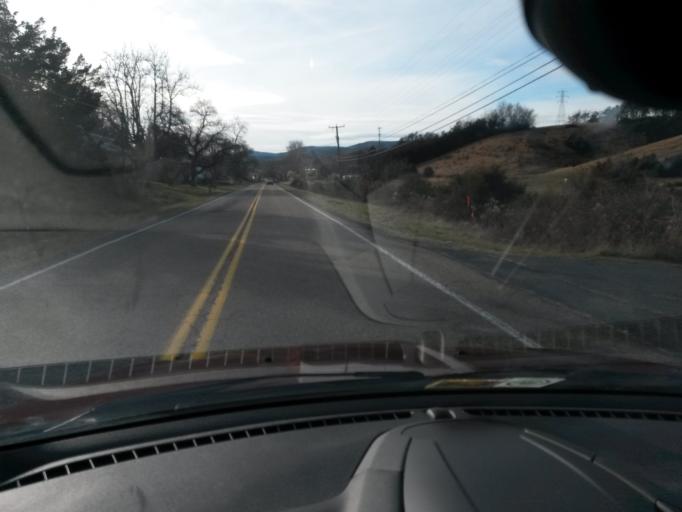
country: US
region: Virginia
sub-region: Rockbridge County
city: East Lexington
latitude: 38.0833
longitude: -79.3715
